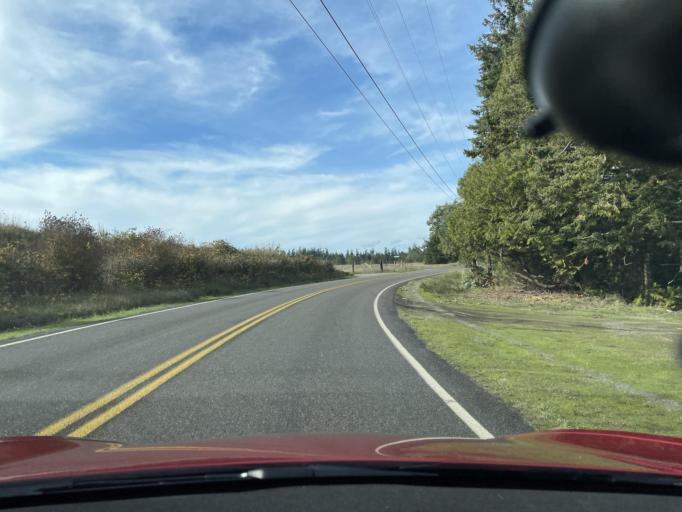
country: US
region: Washington
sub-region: San Juan County
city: Friday Harbor
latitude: 48.5250
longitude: -122.9996
